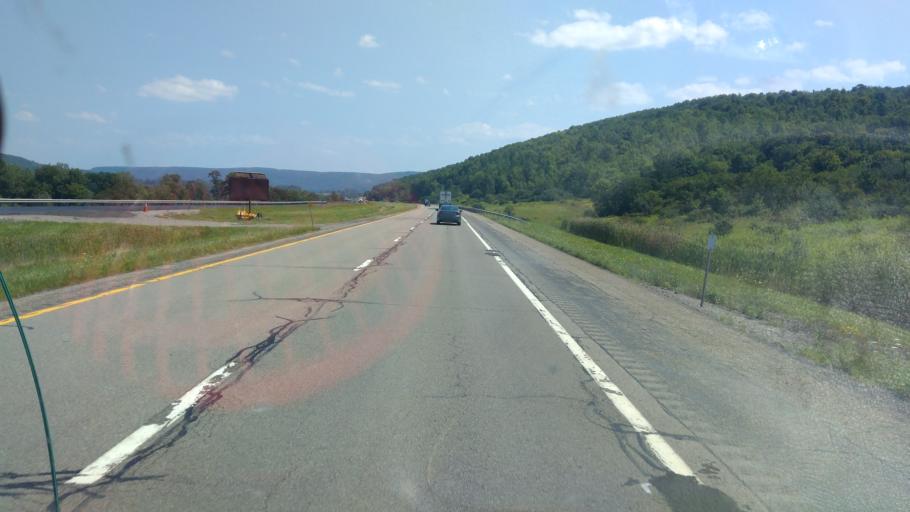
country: US
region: New York
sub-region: Allegany County
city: Alfred
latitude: 42.3168
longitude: -77.7926
